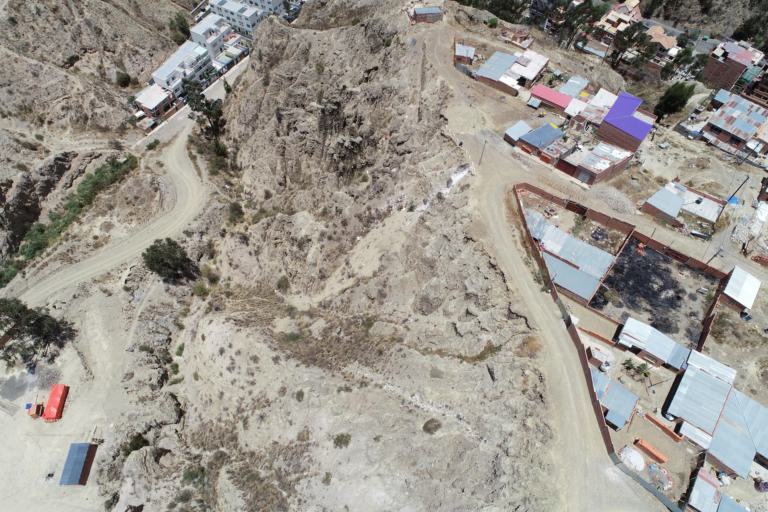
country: BO
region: La Paz
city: La Paz
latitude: -16.5207
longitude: -68.0781
